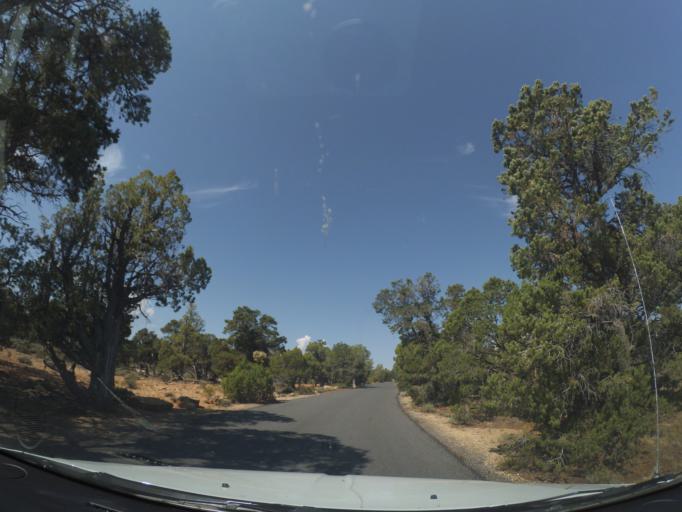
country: US
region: Arizona
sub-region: Coconino County
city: Grand Canyon
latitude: 36.0403
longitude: -111.8241
